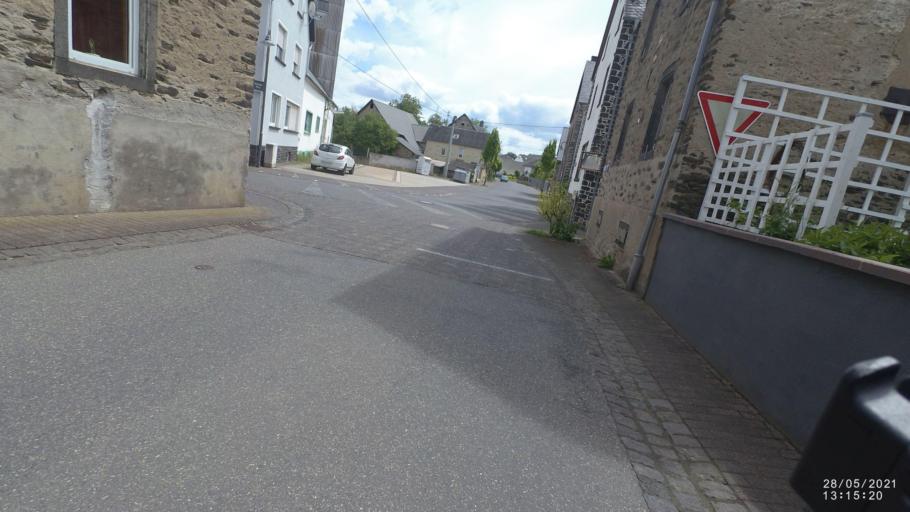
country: DE
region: Rheinland-Pfalz
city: Pillig
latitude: 50.2383
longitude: 7.3116
